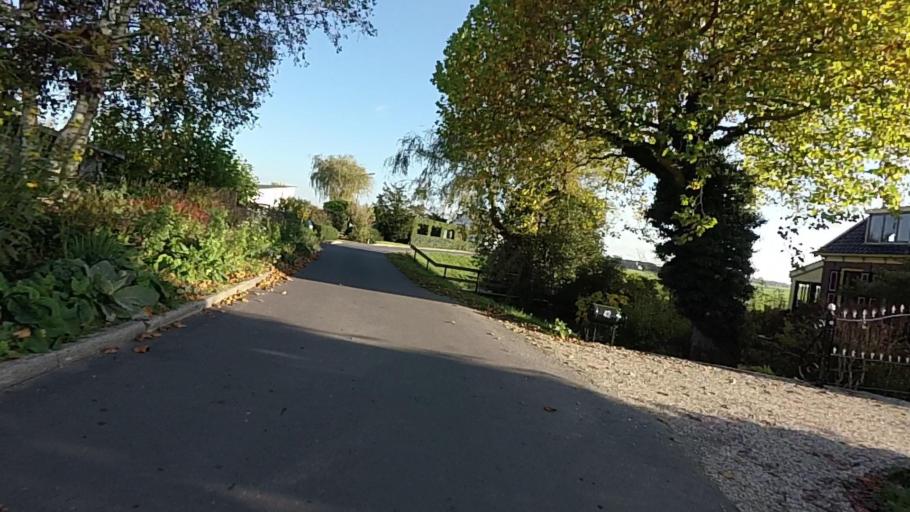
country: NL
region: Utrecht
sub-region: Stichtse Vecht
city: Vreeland
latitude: 52.2570
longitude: 5.0301
